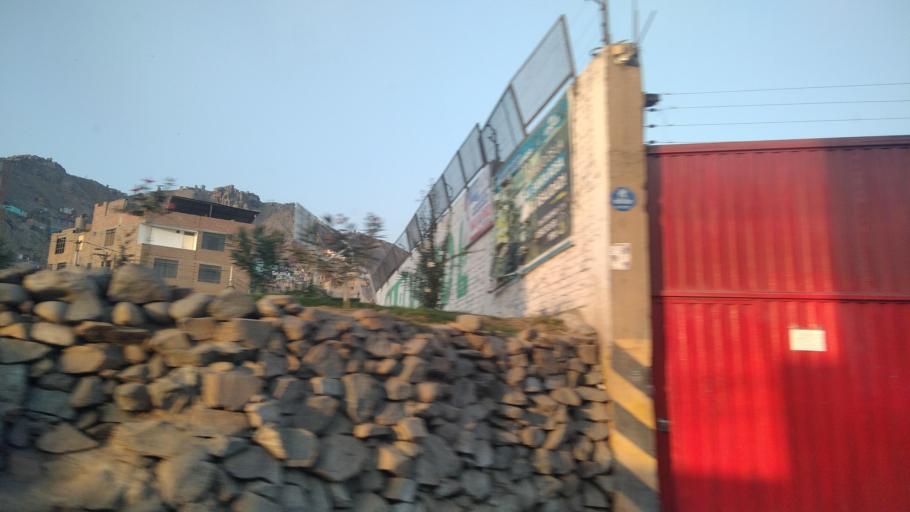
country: PE
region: Lima
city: Lima
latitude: -12.0133
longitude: -76.9944
